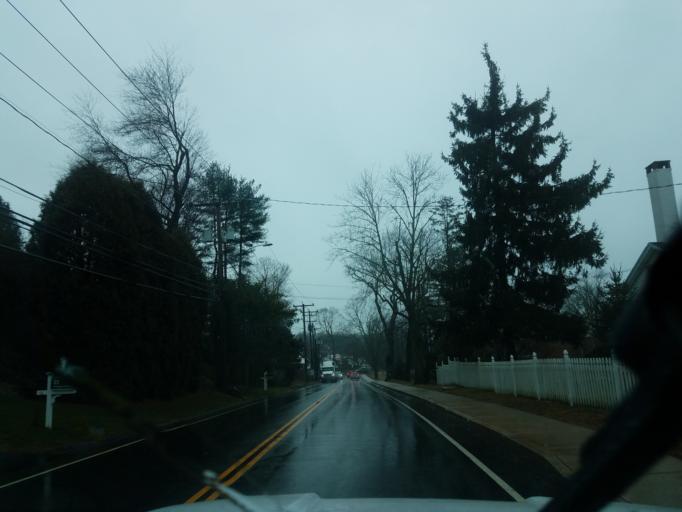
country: US
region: Connecticut
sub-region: Fairfield County
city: Darien
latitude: 41.0619
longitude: -73.4877
